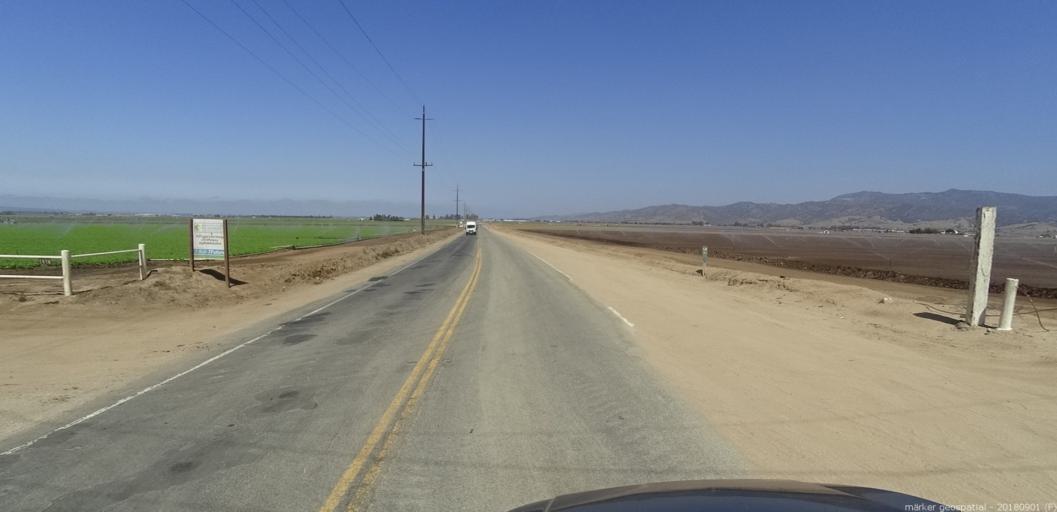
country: US
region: California
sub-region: Monterey County
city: Chualar
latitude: 36.5904
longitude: -121.5024
